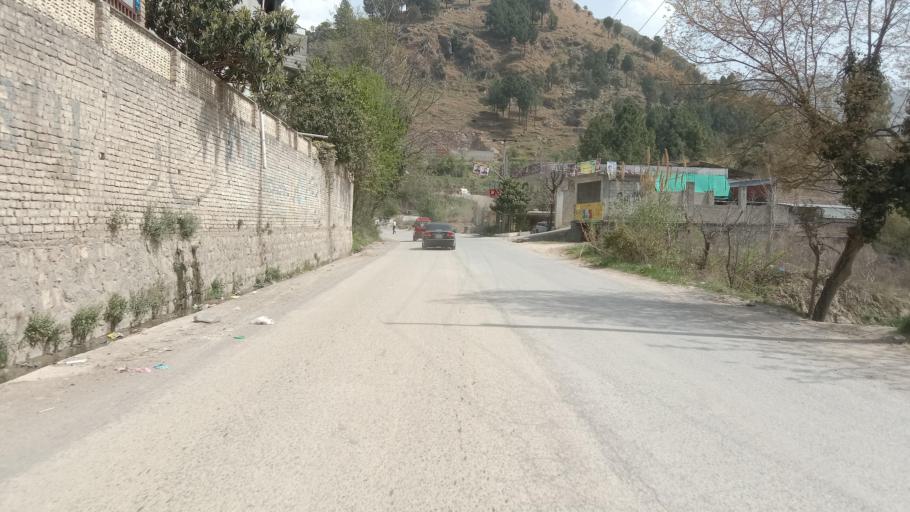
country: PK
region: Khyber Pakhtunkhwa
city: Abbottabad
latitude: 34.1449
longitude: 73.2690
